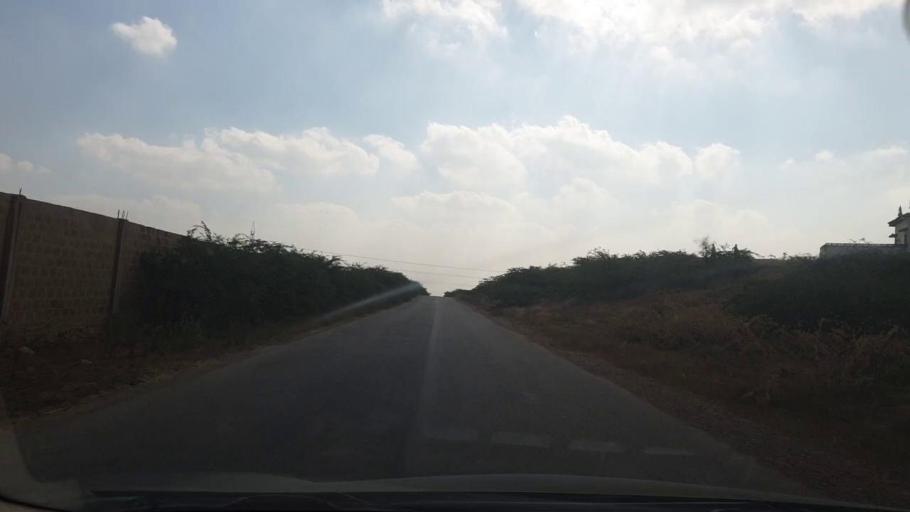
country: PK
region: Sindh
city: Malir Cantonment
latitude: 25.0133
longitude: 67.3529
